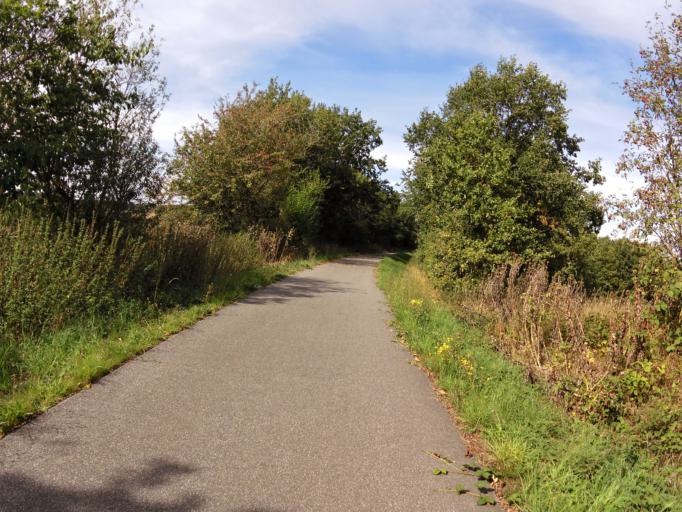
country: DE
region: Rheinland-Pfalz
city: Lichtenborn
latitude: 50.1233
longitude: 6.2627
